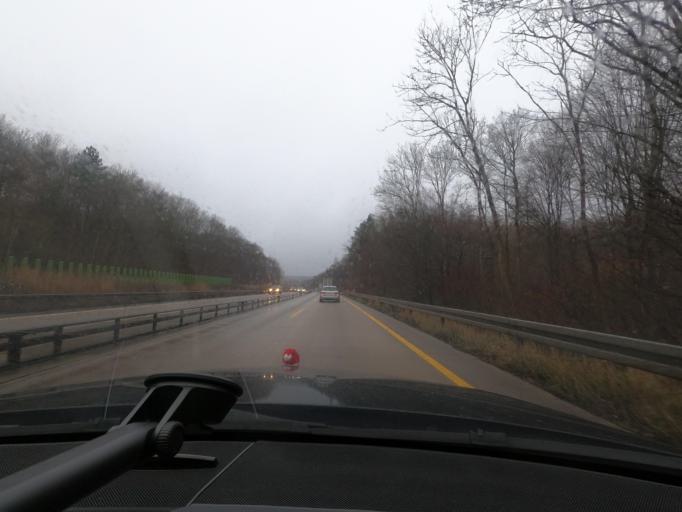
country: DE
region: Lower Saxony
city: Holle
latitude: 52.1145
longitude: 10.1287
